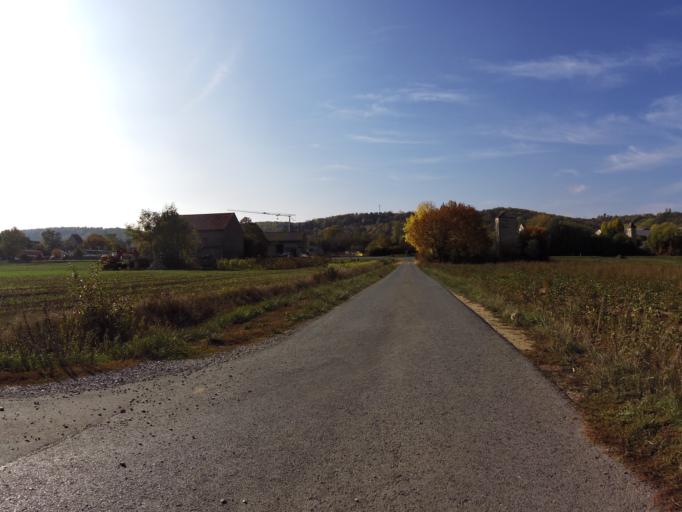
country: DE
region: Bavaria
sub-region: Regierungsbezirk Unterfranken
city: Winterhausen
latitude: 49.7133
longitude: 10.0111
